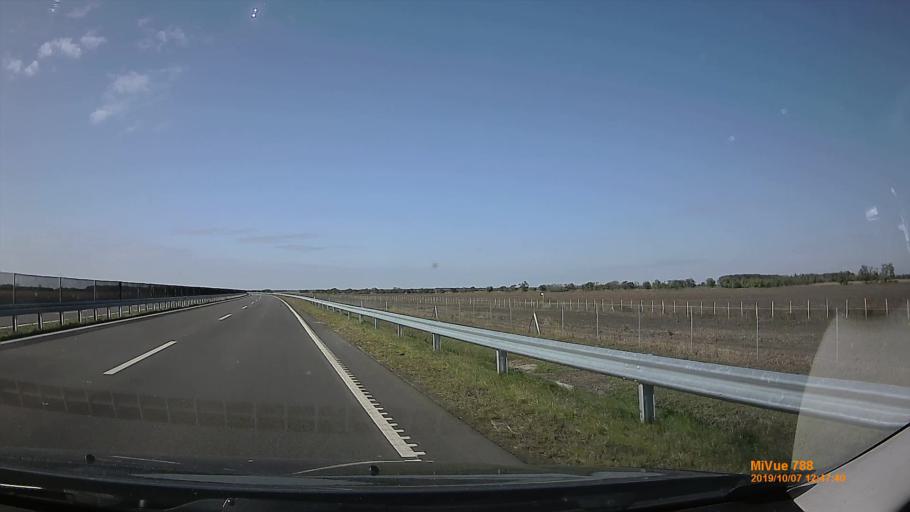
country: HU
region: Jasz-Nagykun-Szolnok
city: Cserkeszolo
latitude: 46.8817
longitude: 20.2377
